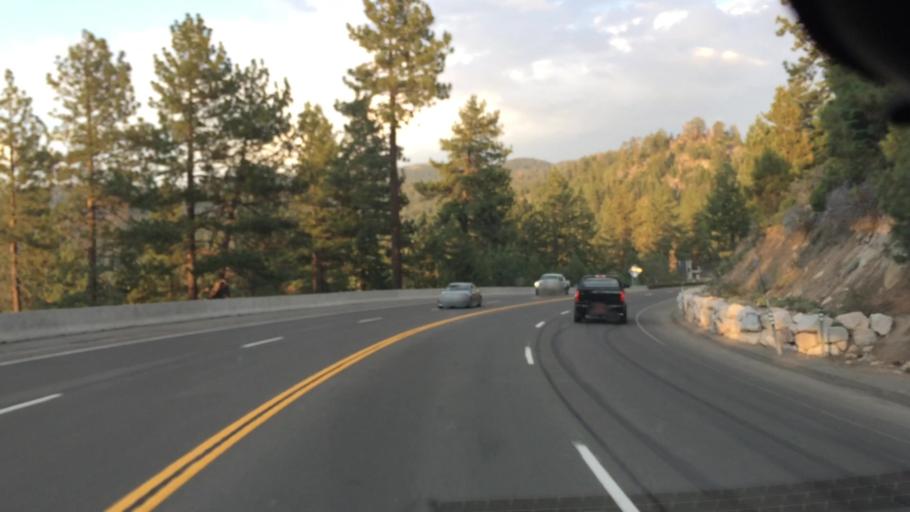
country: US
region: Nevada
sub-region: Douglas County
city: Kingsbury
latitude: 39.0028
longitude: -119.9546
